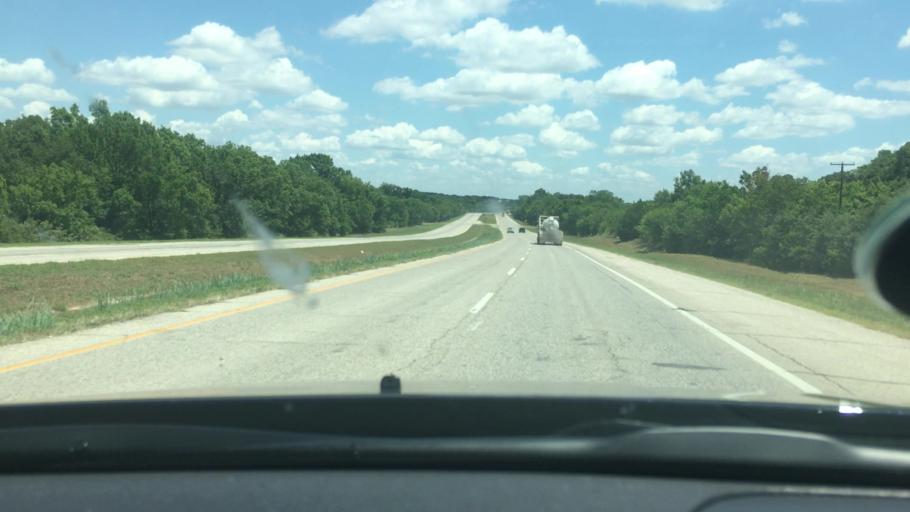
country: US
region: Oklahoma
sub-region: Carter County
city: Wilson
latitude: 34.1729
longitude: -97.3805
